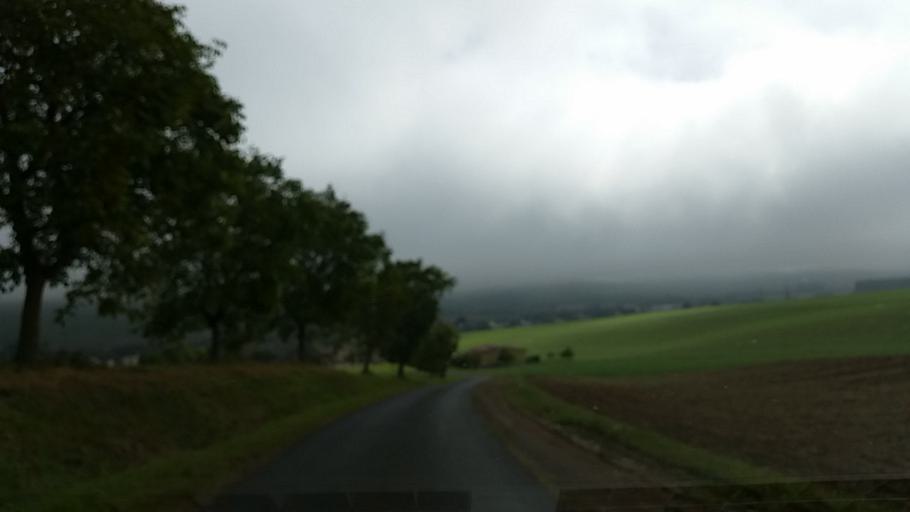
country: DE
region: Bavaria
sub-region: Regierungsbezirk Unterfranken
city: Himmelstadt
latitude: 49.9294
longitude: 9.7907
